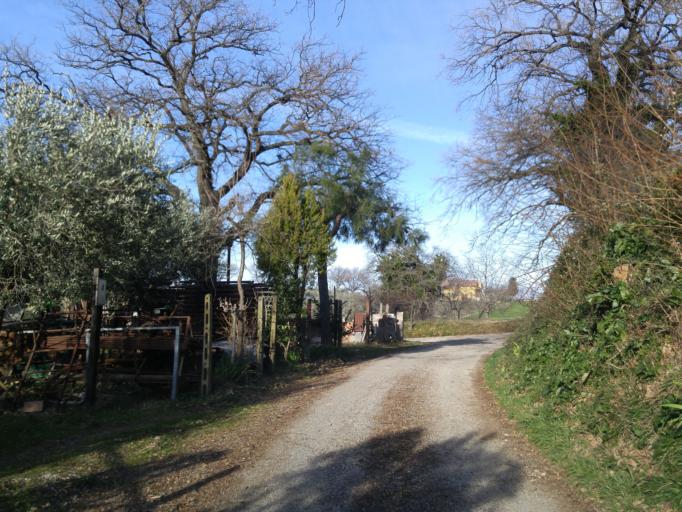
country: IT
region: The Marches
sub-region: Provincia di Pesaro e Urbino
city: Cartoceto
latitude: 43.7757
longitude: 12.8924
